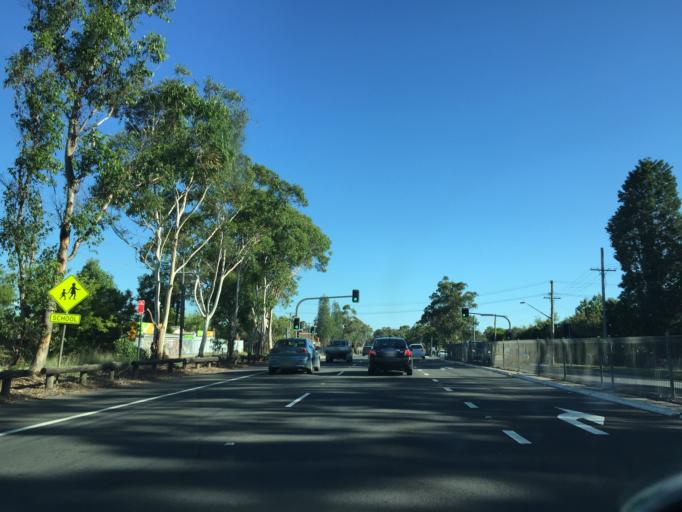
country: AU
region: New South Wales
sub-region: Blue Mountains Municipality
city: Glenbrook
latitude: -33.7554
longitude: 150.6118
